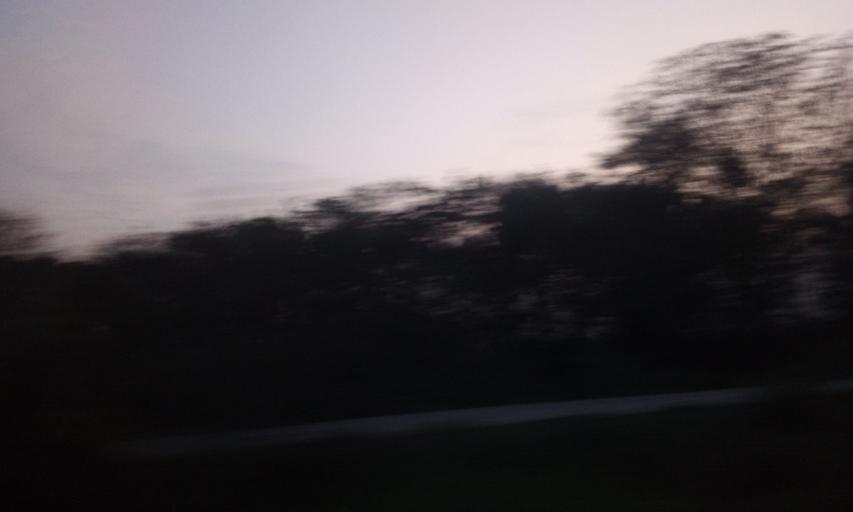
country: TH
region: Sing Buri
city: Sing Buri
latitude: 14.8282
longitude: 100.4049
